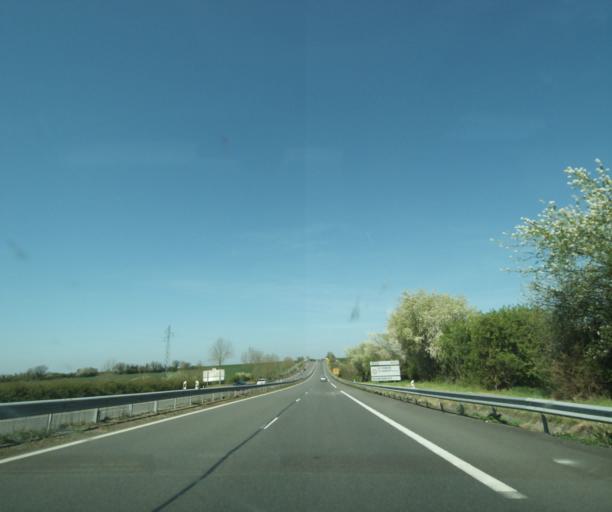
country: FR
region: Bourgogne
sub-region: Departement de la Nievre
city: Chaulgnes
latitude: 47.1251
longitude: 3.0513
